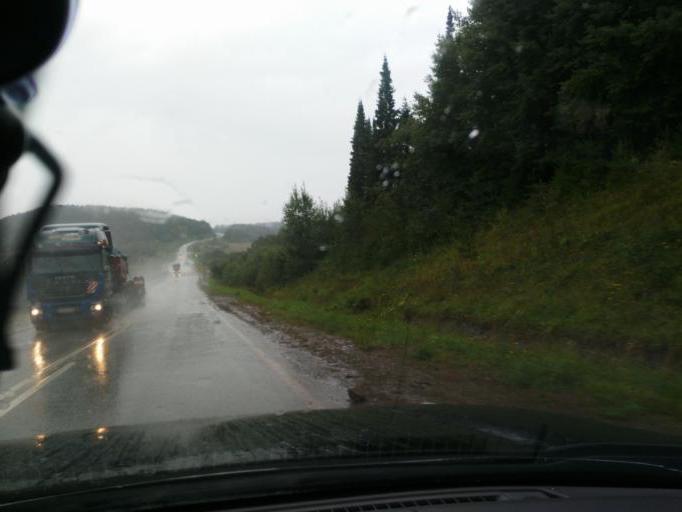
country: RU
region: Perm
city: Osa
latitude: 57.2964
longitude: 55.6126
